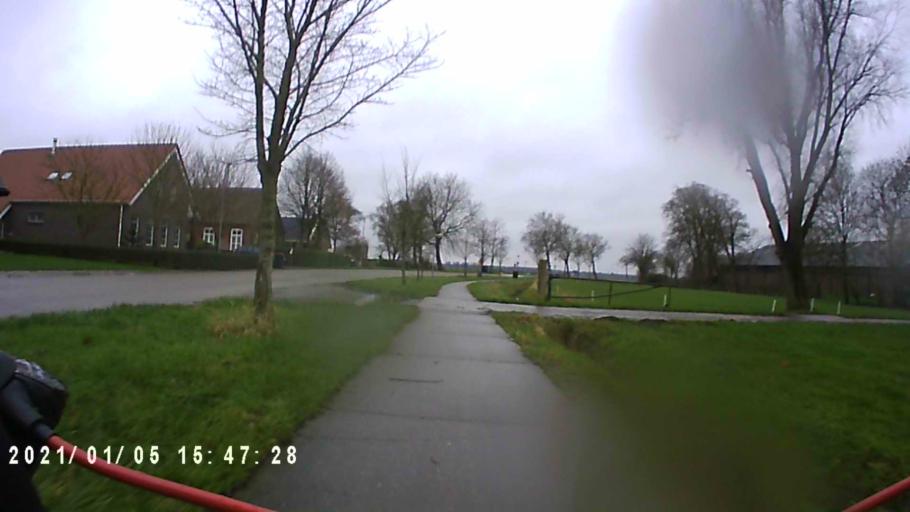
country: NL
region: Groningen
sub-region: Gemeente  Oldambt
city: Winschoten
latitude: 53.2027
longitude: 7.1150
